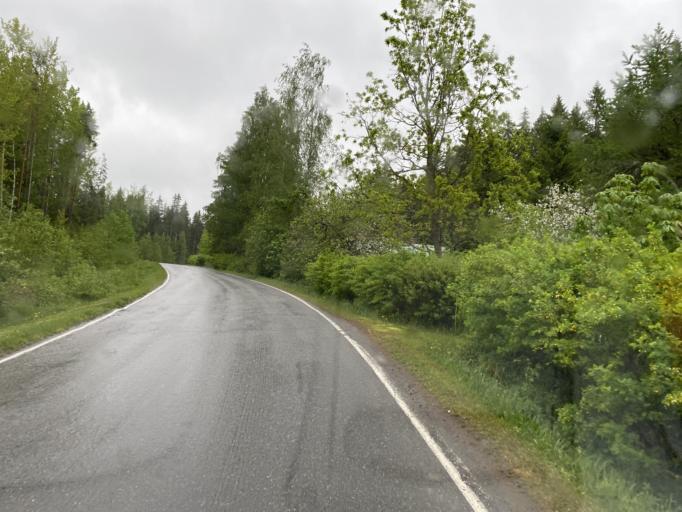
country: FI
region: Pirkanmaa
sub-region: Etelae-Pirkanmaa
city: Urjala
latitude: 60.9680
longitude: 23.5252
